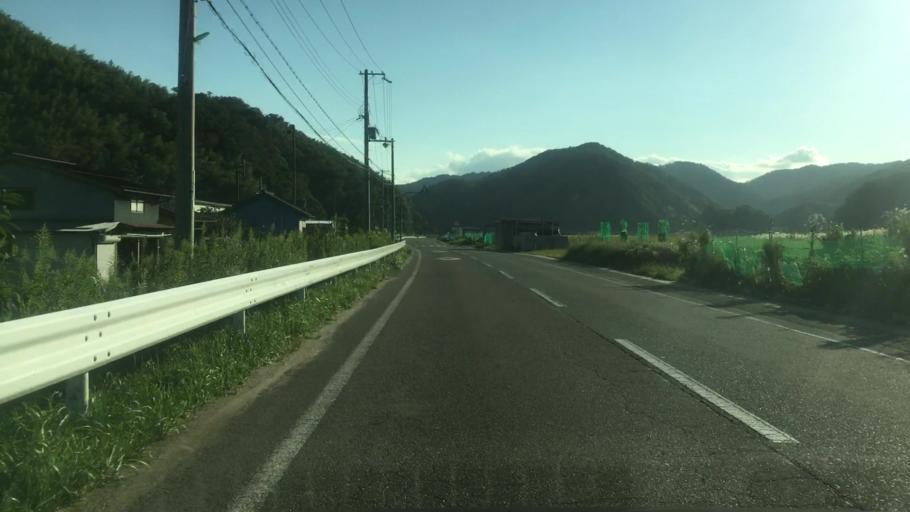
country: JP
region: Hyogo
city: Toyooka
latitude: 35.6139
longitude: 134.8115
